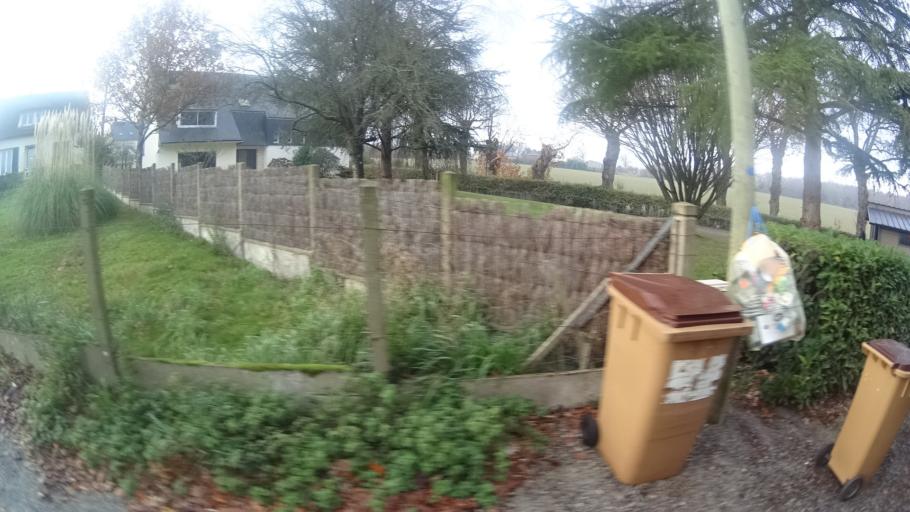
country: FR
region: Pays de la Loire
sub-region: Departement de la Loire-Atlantique
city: Avessac
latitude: 47.6544
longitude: -1.9941
